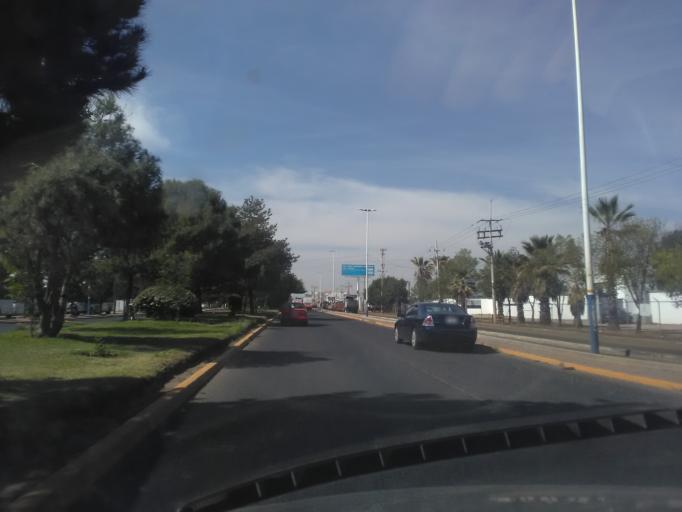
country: MX
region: Durango
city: Victoria de Durango
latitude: 24.0603
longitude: -104.6090
